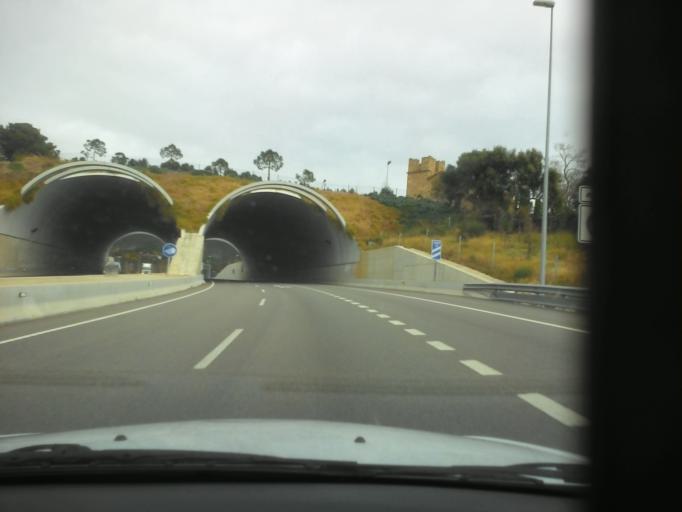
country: ES
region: Catalonia
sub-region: Provincia de Girona
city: Castell-Platja d'Aro
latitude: 41.8229
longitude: 3.0578
